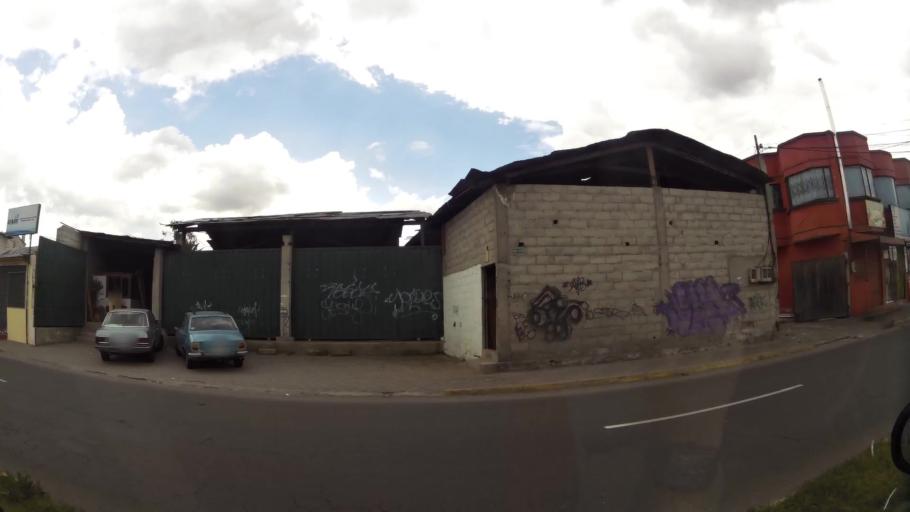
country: EC
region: Pichincha
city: Quito
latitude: -0.0913
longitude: -78.4324
